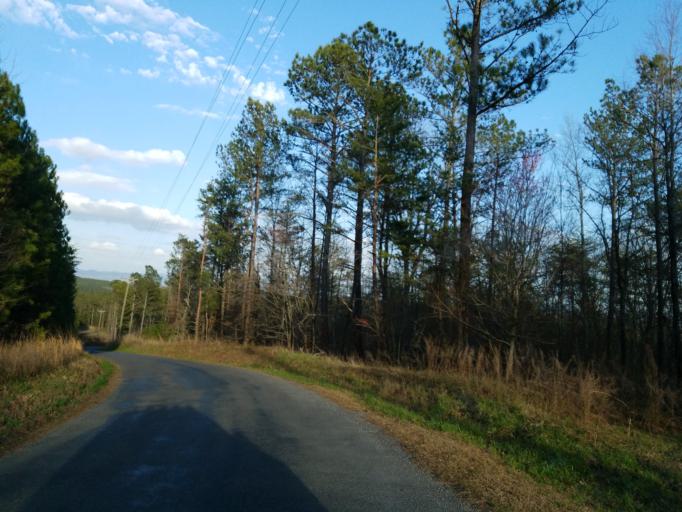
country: US
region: Georgia
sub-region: Pickens County
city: Jasper
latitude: 34.5101
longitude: -84.6108
